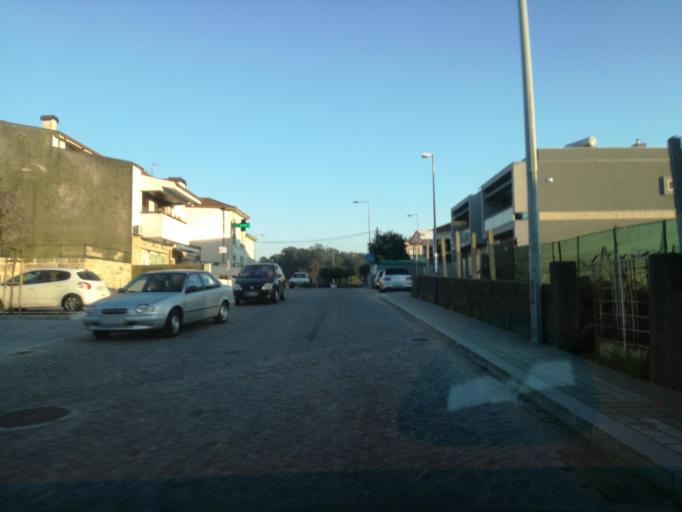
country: PT
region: Porto
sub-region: Maia
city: Milheiros
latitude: 41.2141
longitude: -8.5950
